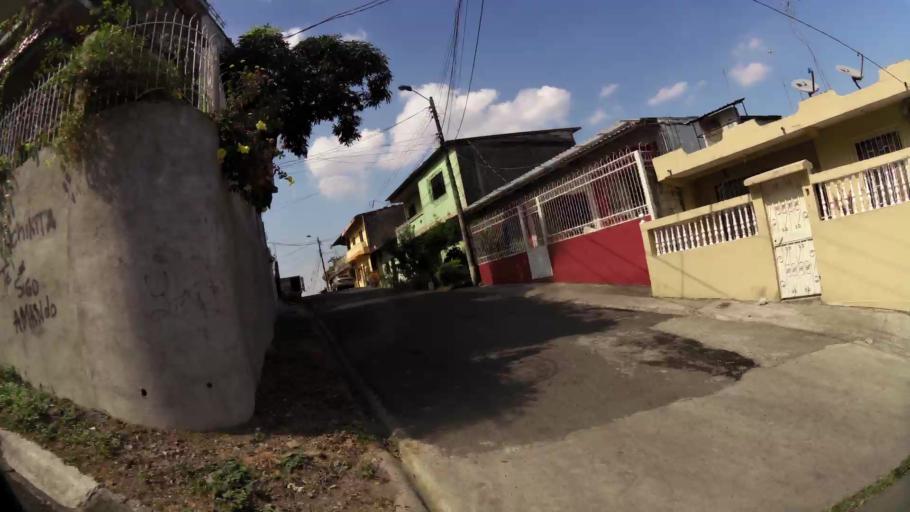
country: EC
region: Guayas
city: Santa Lucia
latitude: -2.1433
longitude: -79.9425
